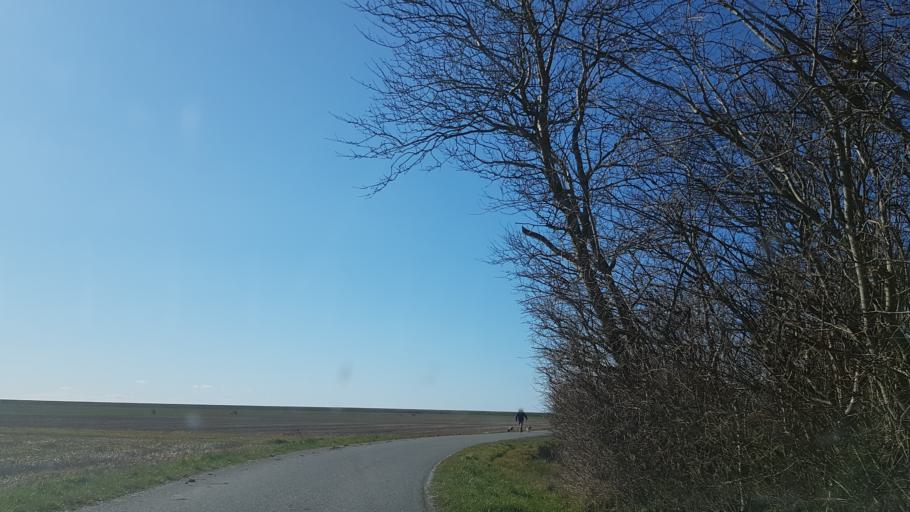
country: DK
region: South Denmark
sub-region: Esbjerg Kommune
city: Ribe
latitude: 55.2571
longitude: 8.6794
